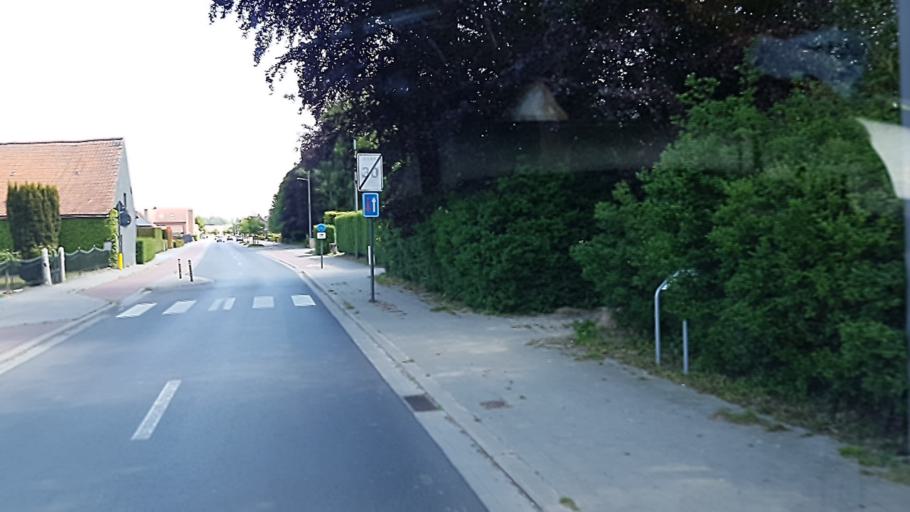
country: BE
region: Flanders
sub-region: Provincie West-Vlaanderen
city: Avelgem
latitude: 50.8191
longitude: 3.4373
